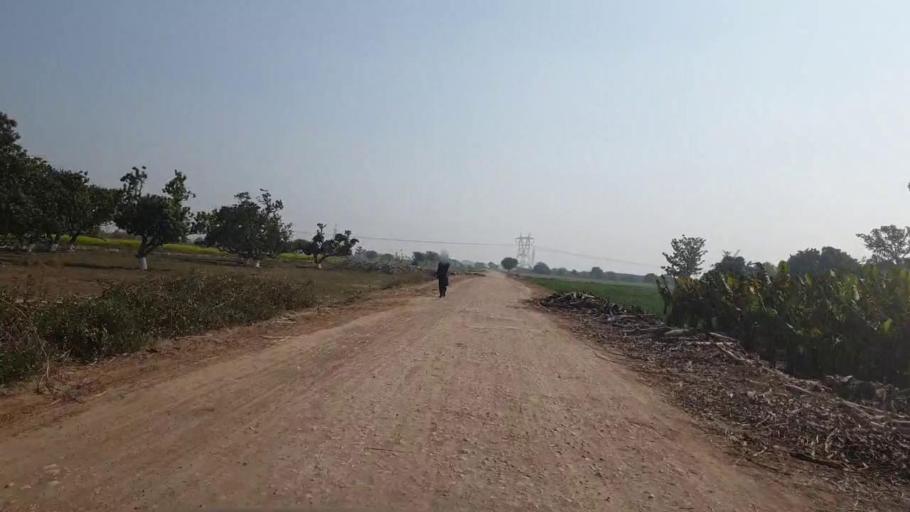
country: PK
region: Sindh
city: Bhit Shah
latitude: 25.7253
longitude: 68.5361
